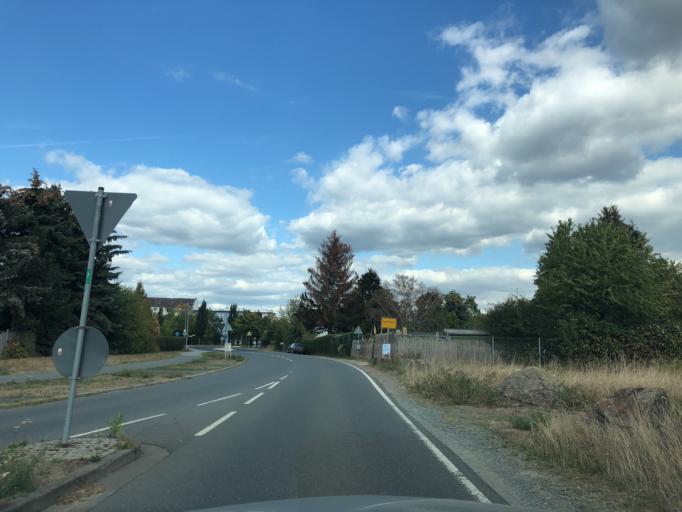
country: DE
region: Hesse
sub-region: Regierungsbezirk Darmstadt
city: Erzhausen
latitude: 49.9635
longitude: 8.6549
